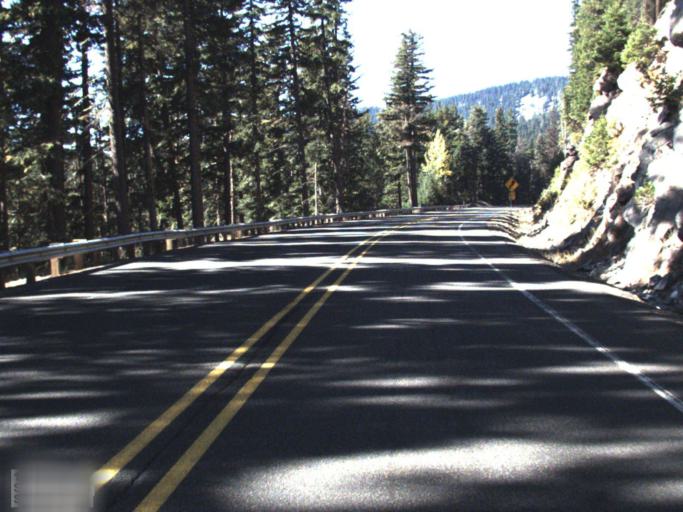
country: US
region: Washington
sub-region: Yakima County
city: Tieton
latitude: 46.6483
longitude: -121.3682
